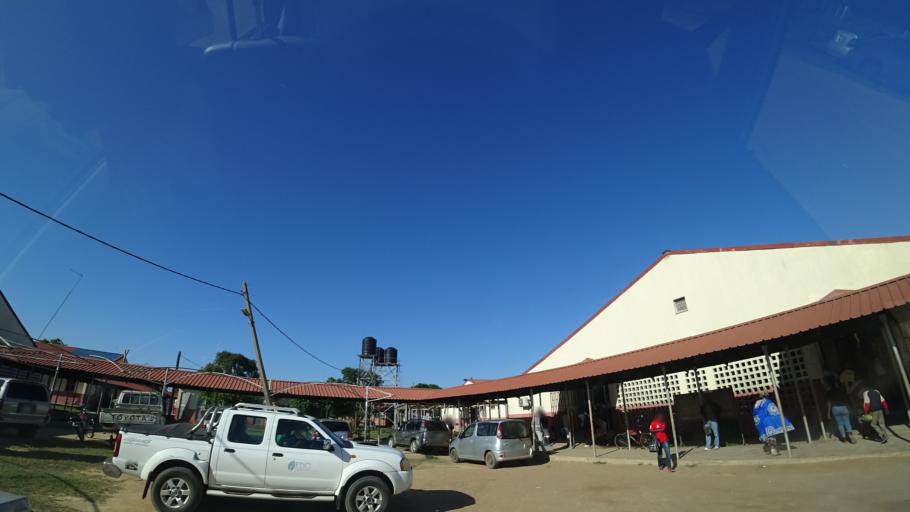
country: MZ
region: Sofala
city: Dondo
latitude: -19.6183
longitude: 34.7409
